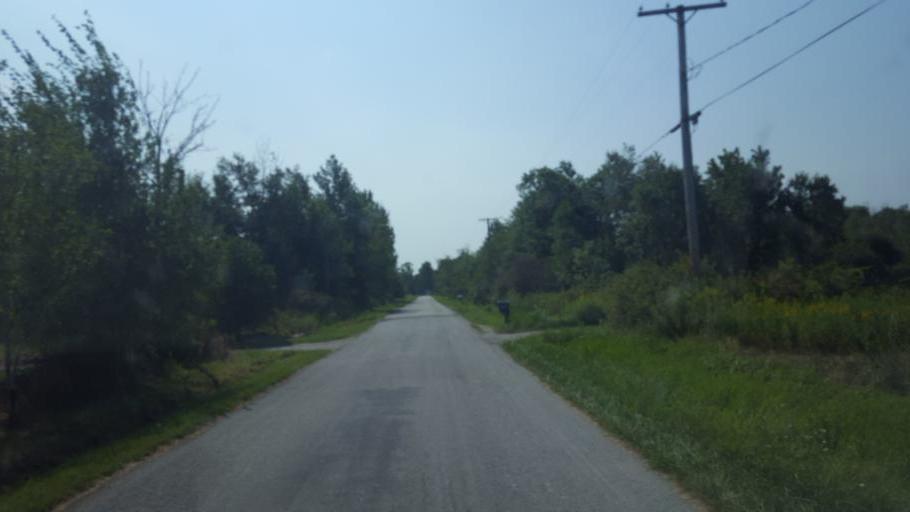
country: US
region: Ohio
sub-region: Ashtabula County
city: Orwell
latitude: 41.5894
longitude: -80.9923
